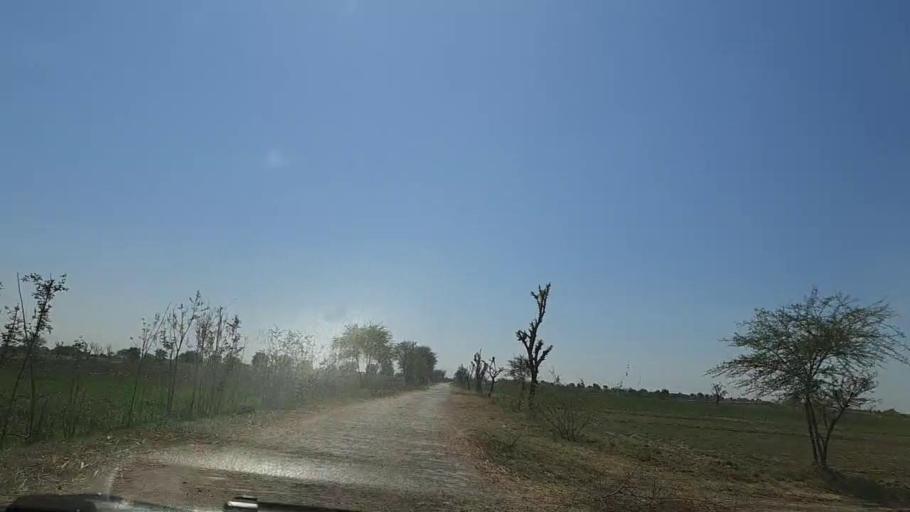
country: PK
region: Sindh
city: Dhoro Naro
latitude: 25.4885
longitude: 69.5439
